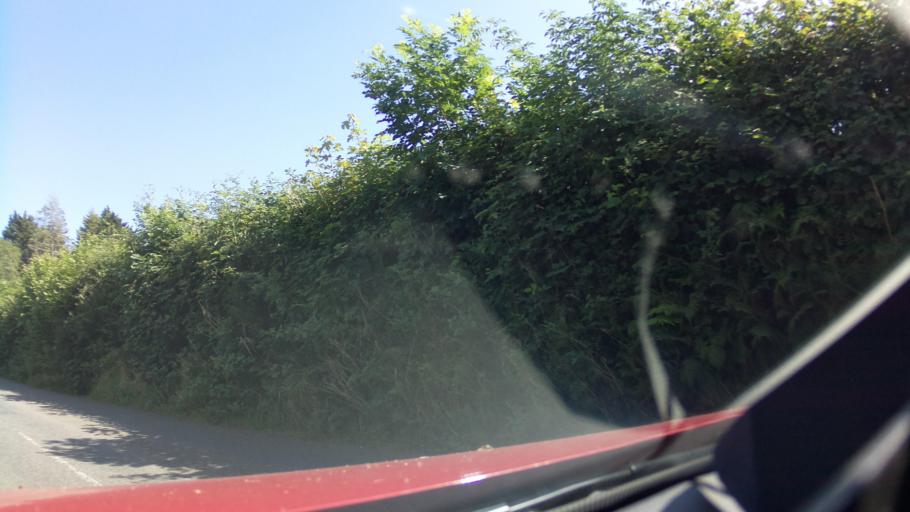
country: GB
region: England
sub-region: Devon
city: Tavistock
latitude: 50.5525
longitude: -4.1252
